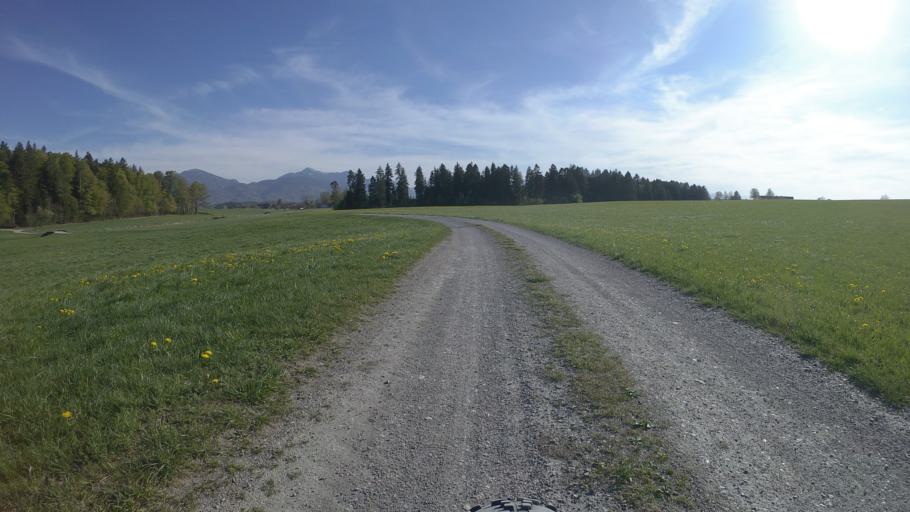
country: DE
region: Bavaria
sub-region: Upper Bavaria
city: Grabenstatt
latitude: 47.8664
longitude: 12.5382
